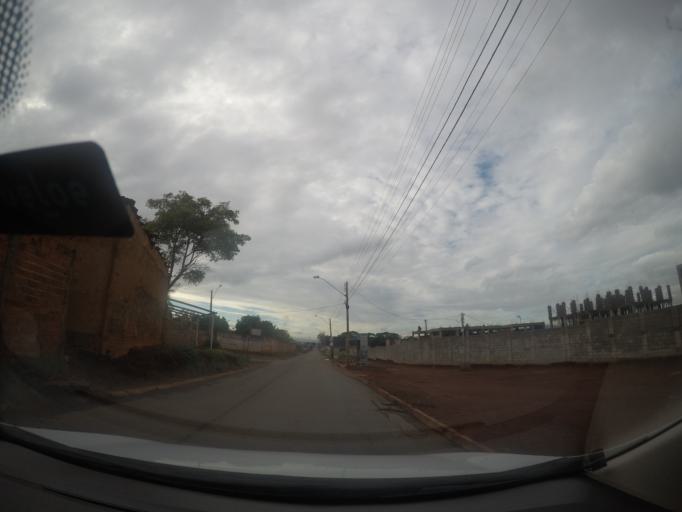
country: BR
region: Goias
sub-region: Goiania
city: Goiania
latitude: -16.6141
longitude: -49.3320
